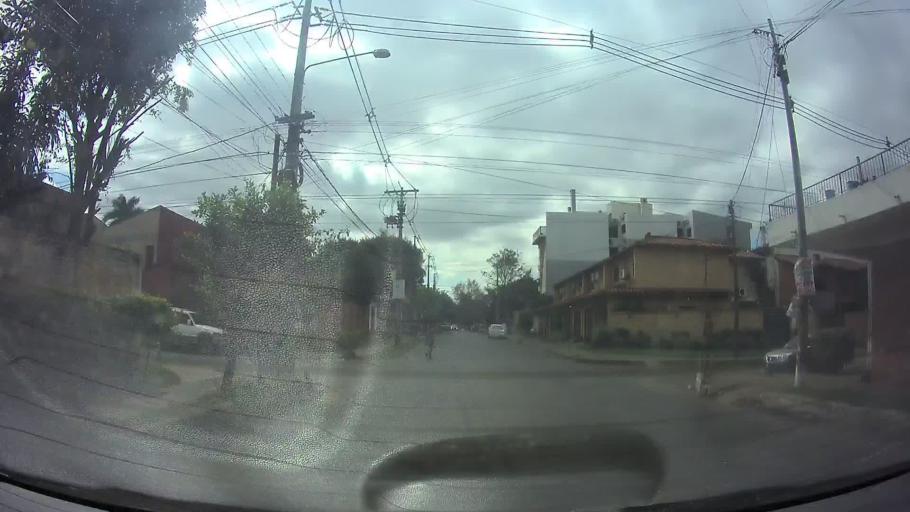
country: PY
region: Central
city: Fernando de la Mora
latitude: -25.3017
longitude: -57.5576
